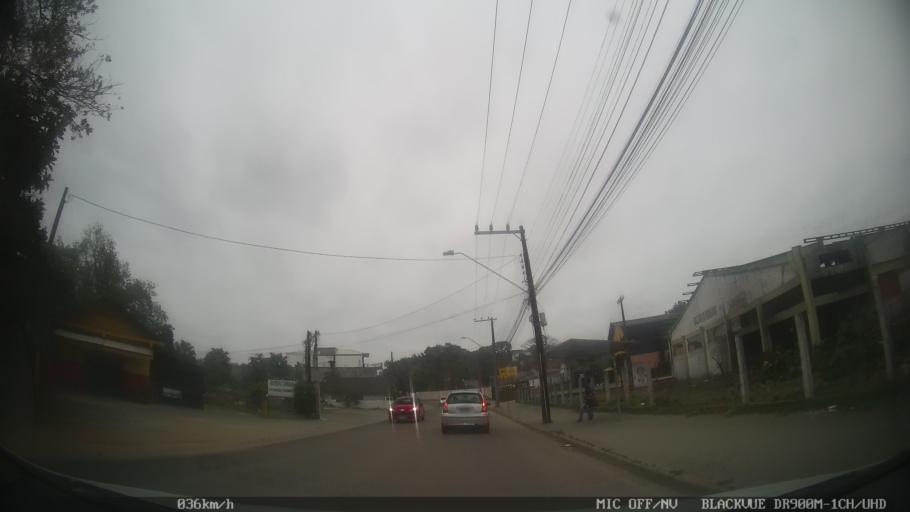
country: BR
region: Santa Catarina
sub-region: Joinville
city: Joinville
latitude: -26.3620
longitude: -48.8381
